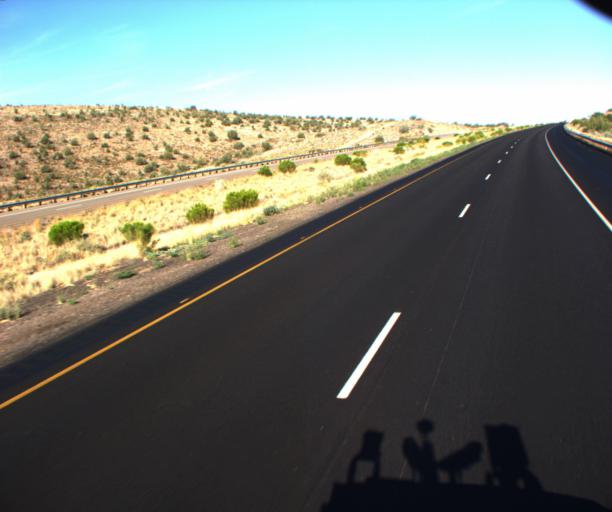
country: US
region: Arizona
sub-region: Mohave County
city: New Kingman-Butler
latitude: 35.1604
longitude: -113.6479
